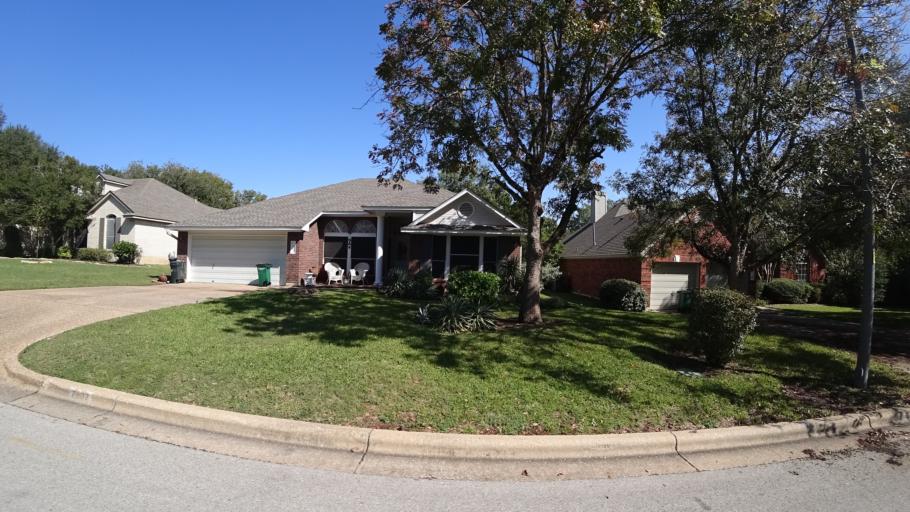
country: US
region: Texas
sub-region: Travis County
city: Shady Hollow
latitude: 30.2186
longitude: -97.8583
